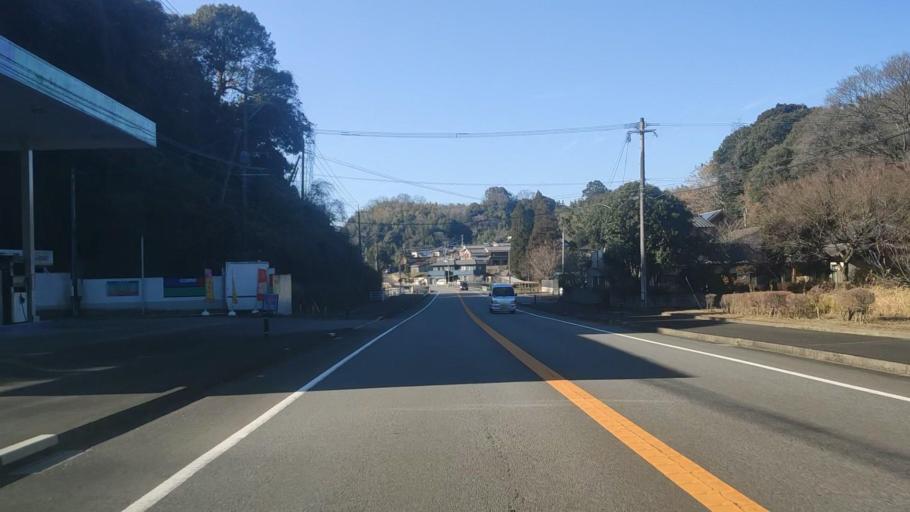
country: JP
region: Oita
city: Usuki
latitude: 33.0637
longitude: 131.6631
